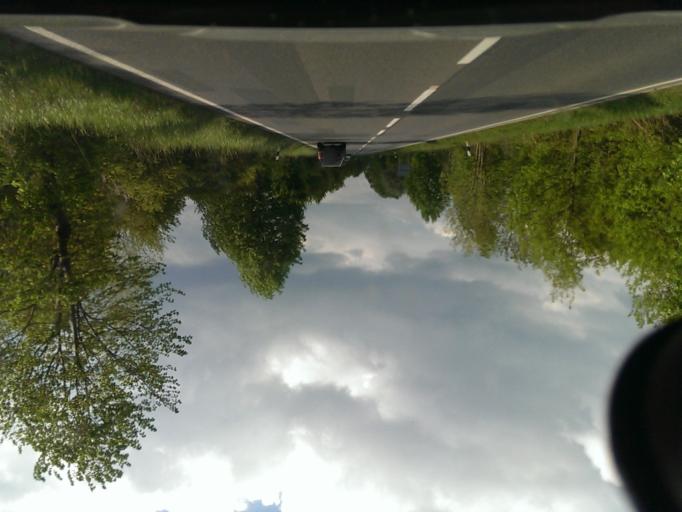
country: DE
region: Lower Saxony
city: Banteln
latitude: 52.0770
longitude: 9.7438
